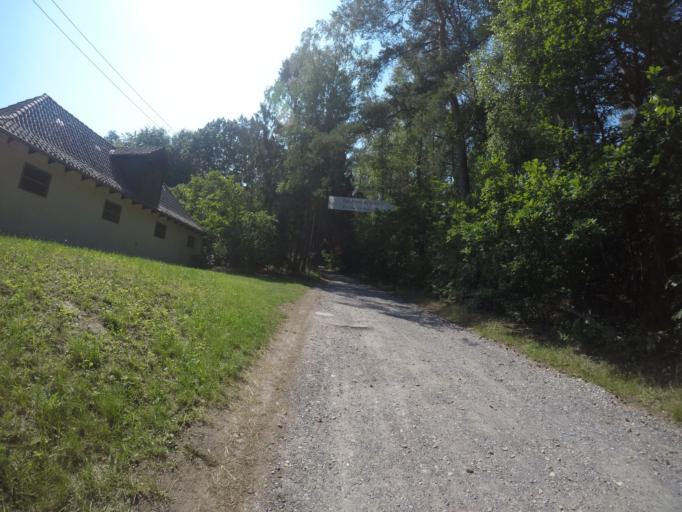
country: DE
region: Lower Saxony
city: Buchholz in der Nordheide
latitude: 53.3078
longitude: 9.8190
